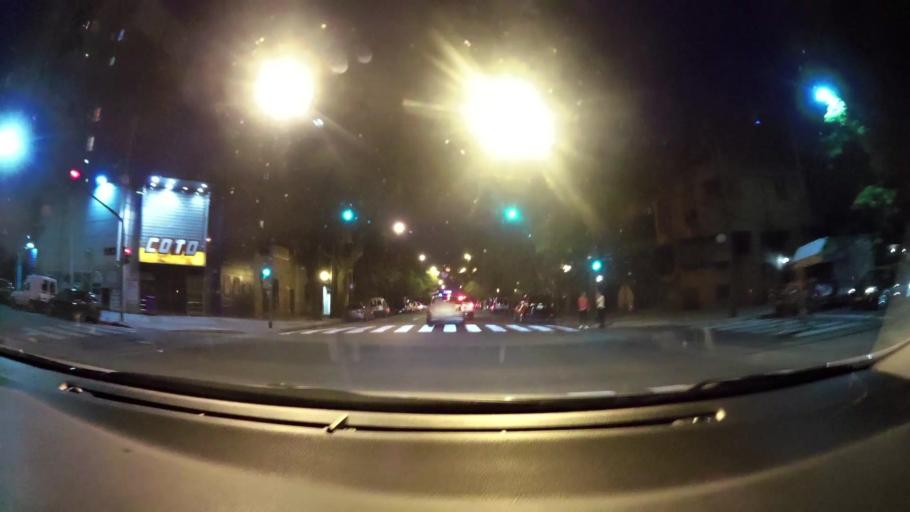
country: AR
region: Buenos Aires F.D.
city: Colegiales
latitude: -34.5797
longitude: -58.4605
